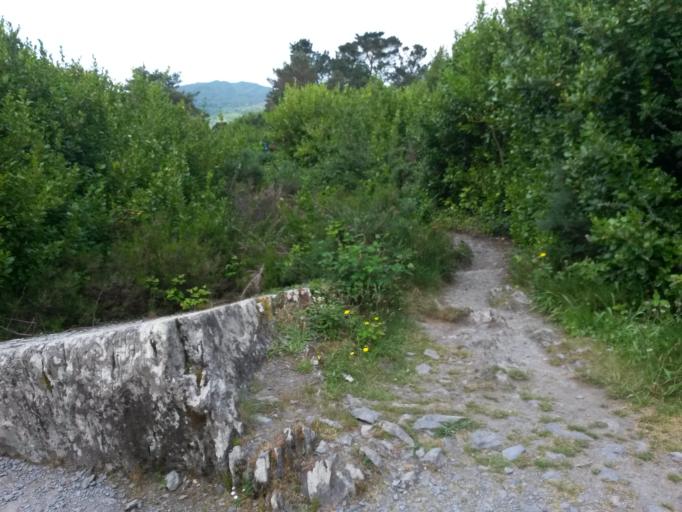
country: IE
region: Munster
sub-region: County Cork
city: Bantry
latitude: 51.7361
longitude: -9.5418
